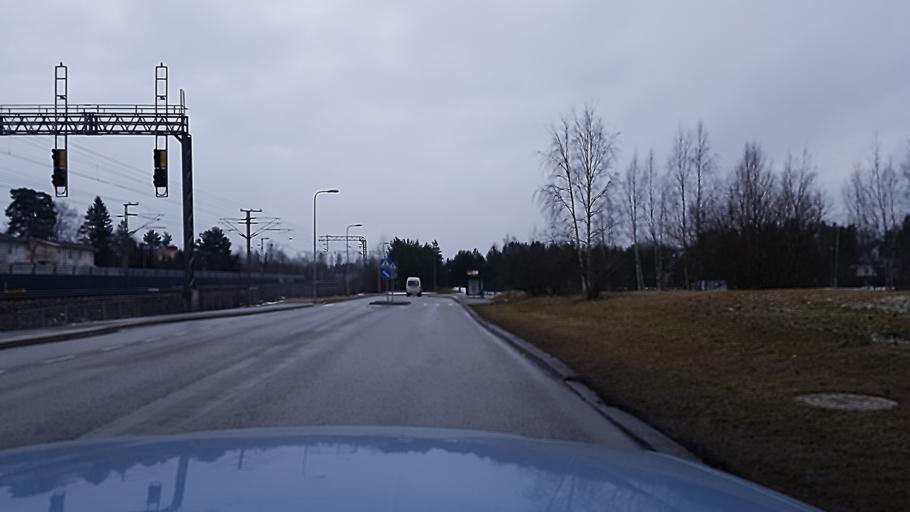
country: FI
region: Uusimaa
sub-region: Helsinki
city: Vantaa
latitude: 60.2689
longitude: 25.0328
